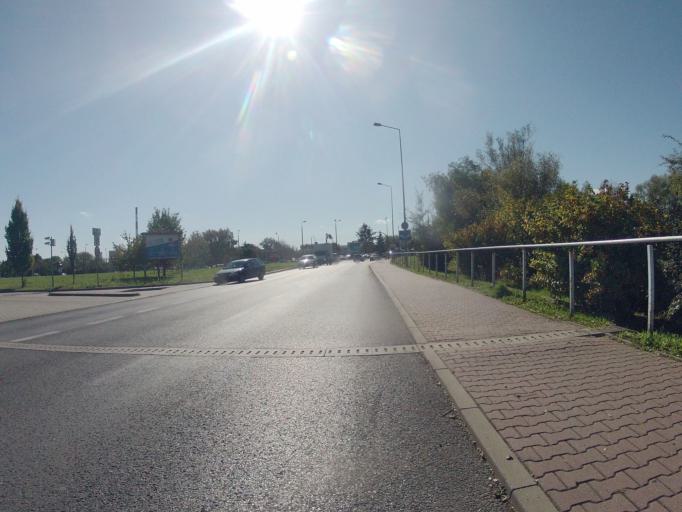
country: PL
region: Lesser Poland Voivodeship
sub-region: Krakow
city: Krakow
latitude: 50.0651
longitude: 19.9875
